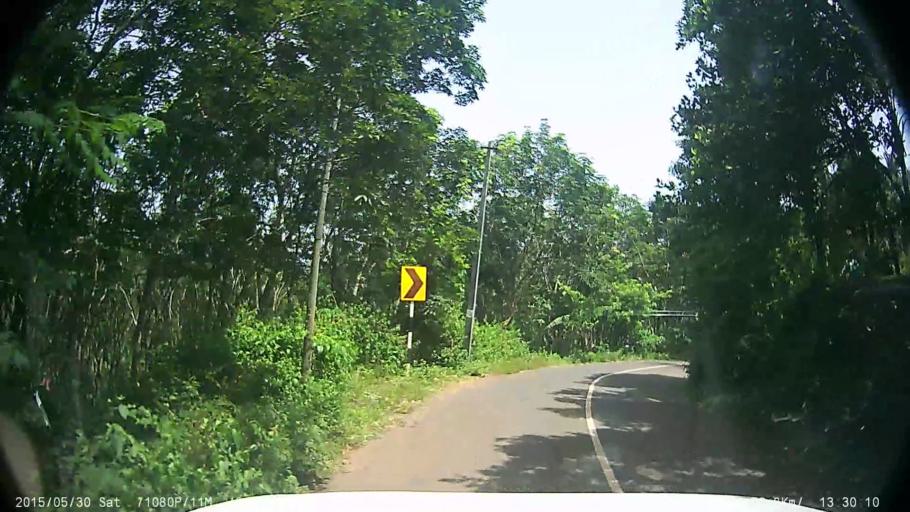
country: IN
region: Kerala
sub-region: Wayanad
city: Panamaram
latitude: 11.8166
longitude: 76.0883
